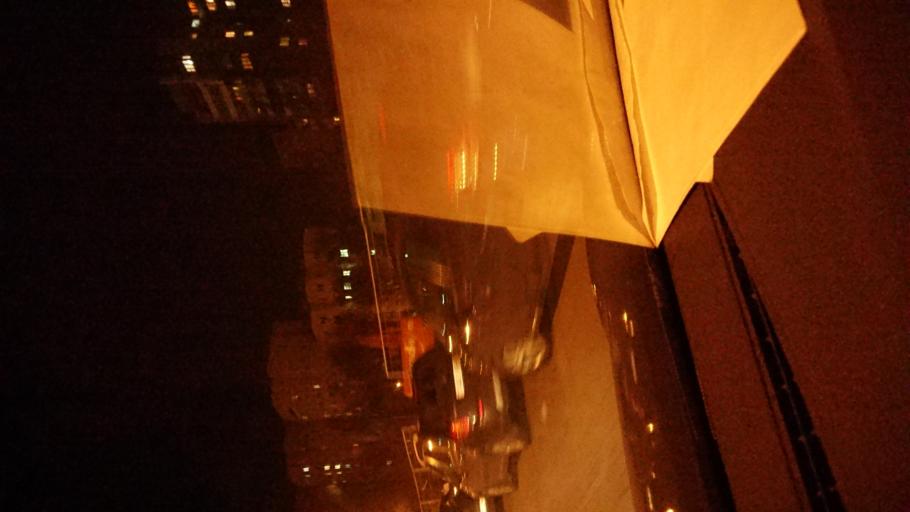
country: BY
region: Minsk
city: Minsk
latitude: 53.9398
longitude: 27.6009
